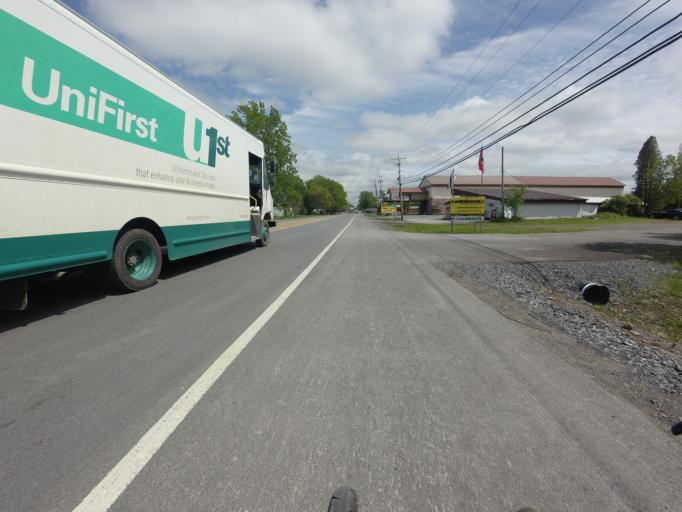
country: CA
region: Ontario
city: Cornwall
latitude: 44.9752
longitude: -74.6719
